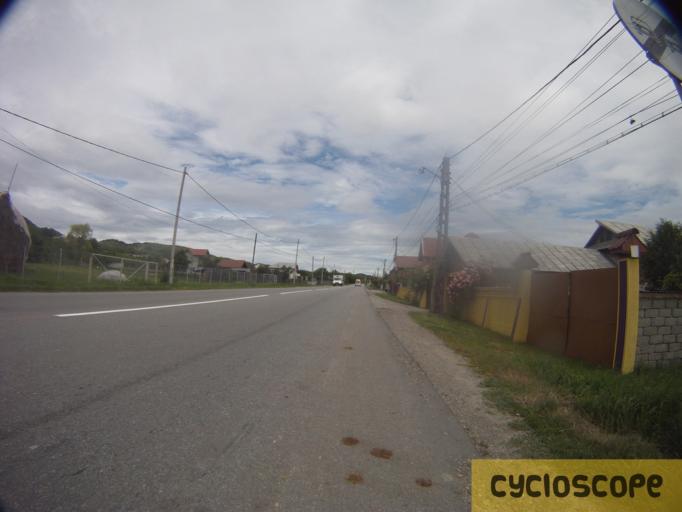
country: RO
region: Valcea
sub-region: Municipiul Ramnicu Valcea
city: Stolniceni
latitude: 45.0564
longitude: 24.2889
